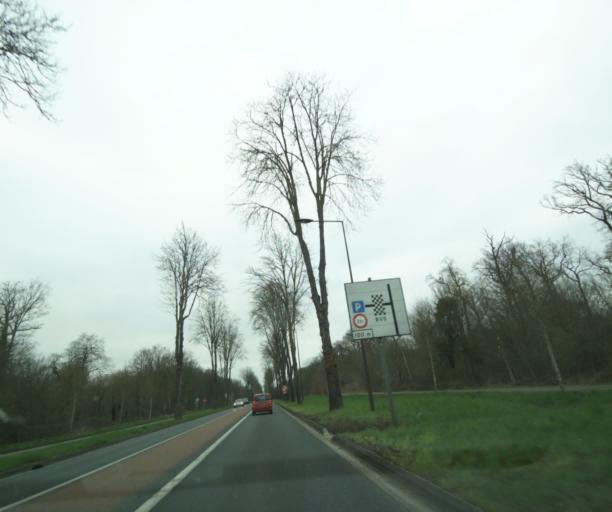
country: FR
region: Ile-de-France
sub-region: Departement des Yvelines
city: Saint-Germain-en-Laye
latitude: 48.9138
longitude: 2.0690
